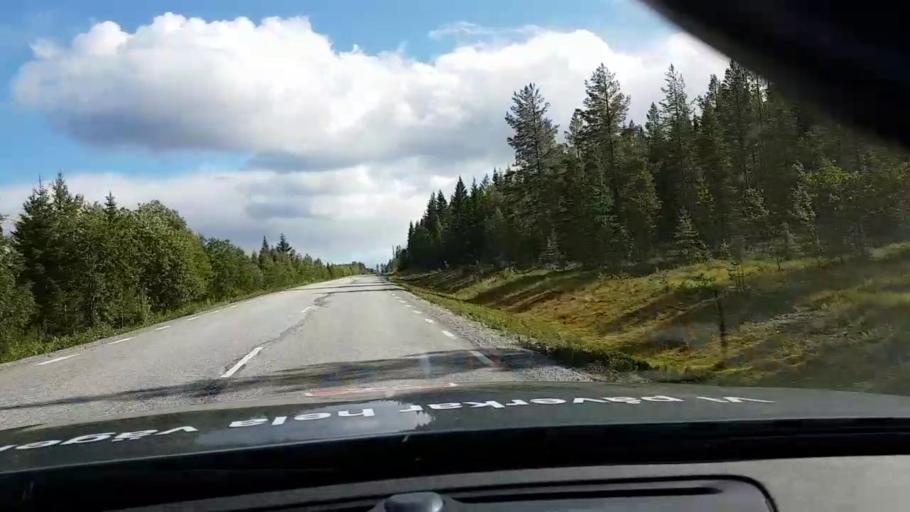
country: SE
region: Vaesterbotten
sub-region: Asele Kommun
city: Asele
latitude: 63.7803
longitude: 17.6644
